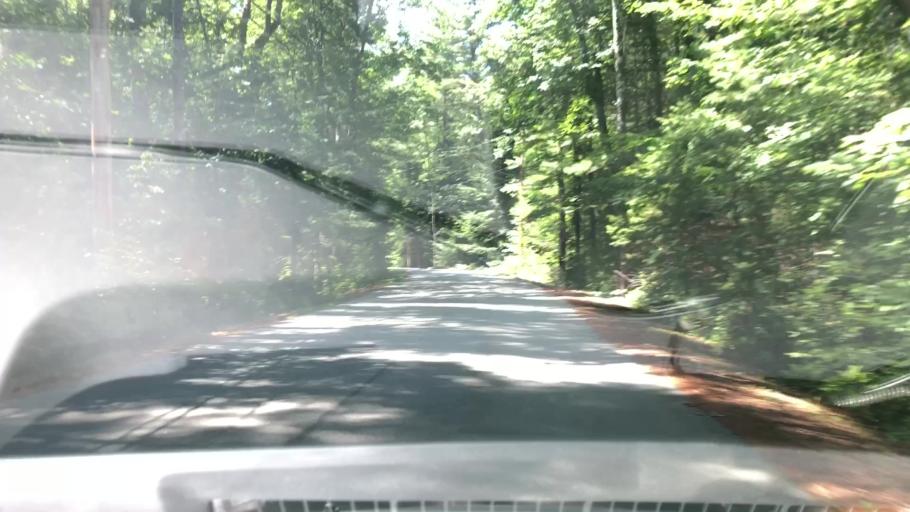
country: US
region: New Hampshire
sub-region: Hillsborough County
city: Milford
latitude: 42.8569
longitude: -71.5891
